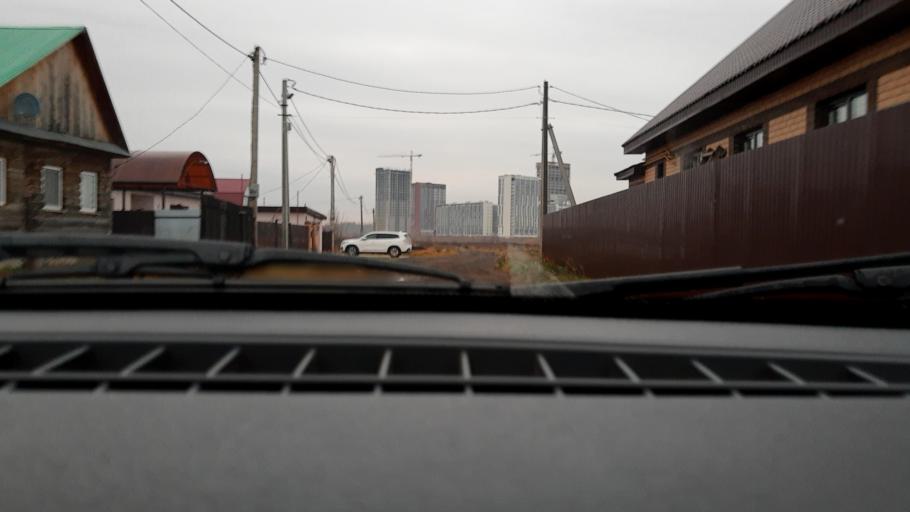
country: RU
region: Bashkortostan
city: Mikhaylovka
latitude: 54.7642
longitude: 55.9048
